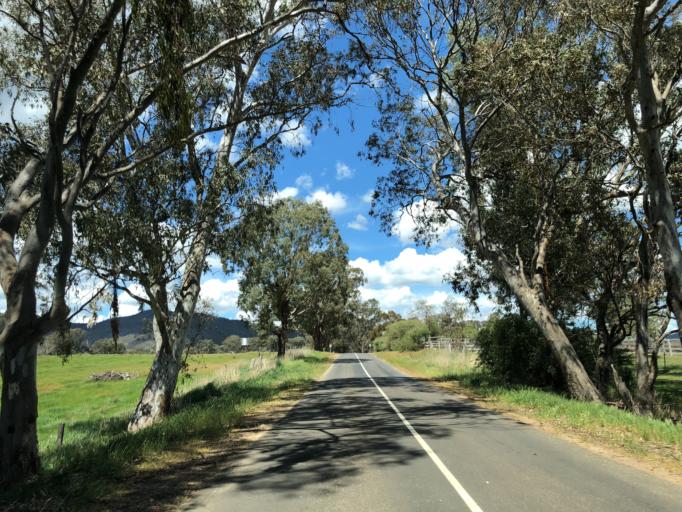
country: AU
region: Victoria
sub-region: Benalla
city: Benalla
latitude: -36.7352
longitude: 146.1124
